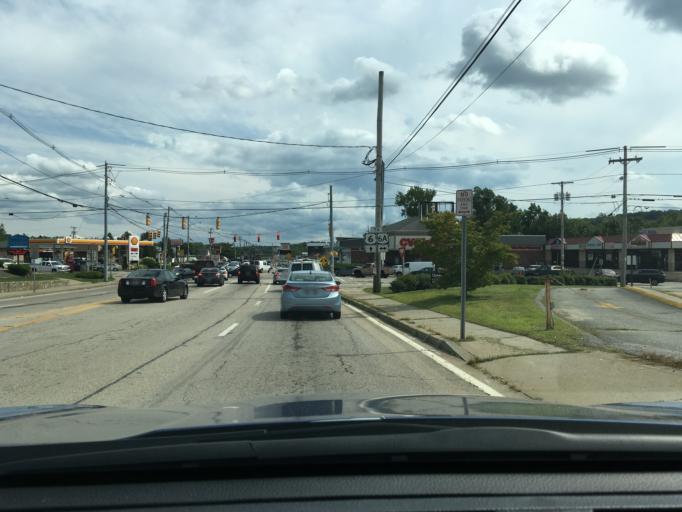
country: US
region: Rhode Island
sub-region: Providence County
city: Johnston
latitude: 41.8246
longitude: -71.4994
